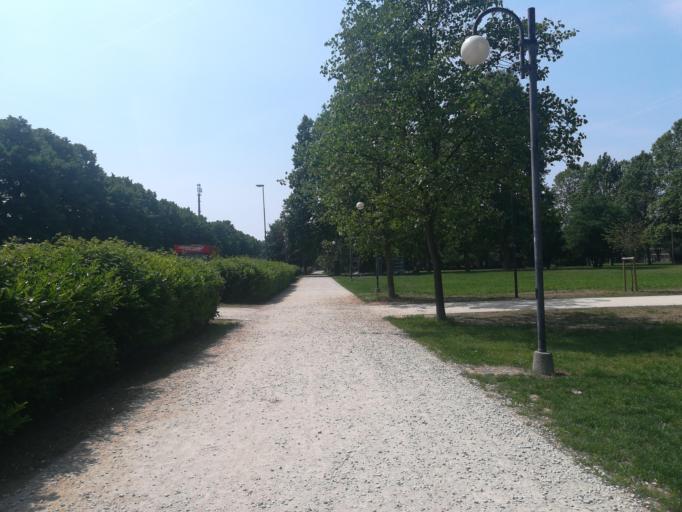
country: IT
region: Piedmont
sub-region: Provincia di Torino
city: Collegno
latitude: 45.0803
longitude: 7.5811
